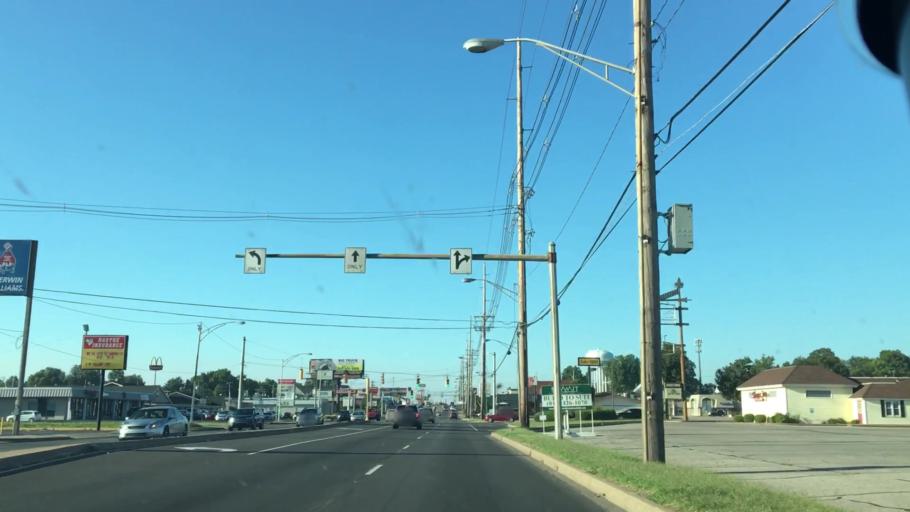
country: US
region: Indiana
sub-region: Vanderburgh County
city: Evansville
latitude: 37.9651
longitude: -87.4926
